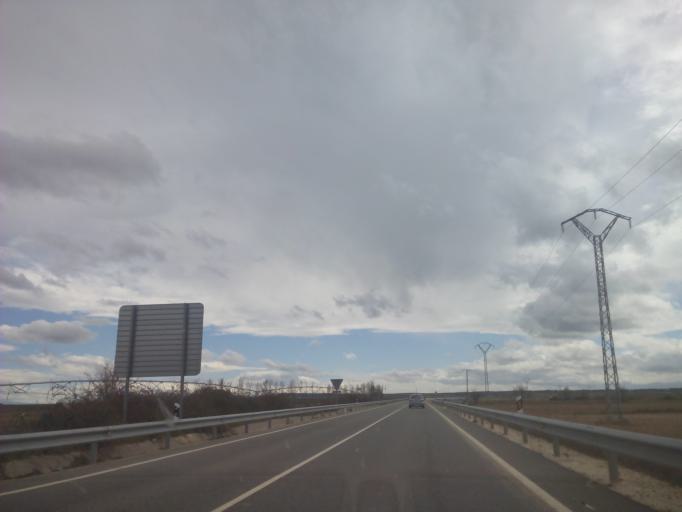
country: ES
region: Castille and Leon
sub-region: Provincia de Salamanca
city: Encinas de Abajo
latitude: 40.9363
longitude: -5.4962
